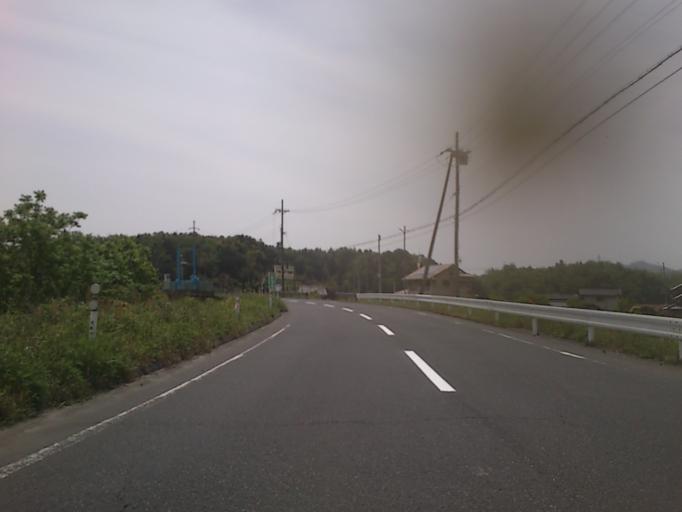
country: JP
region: Kyoto
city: Miyazu
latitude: 35.6415
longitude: 135.0806
